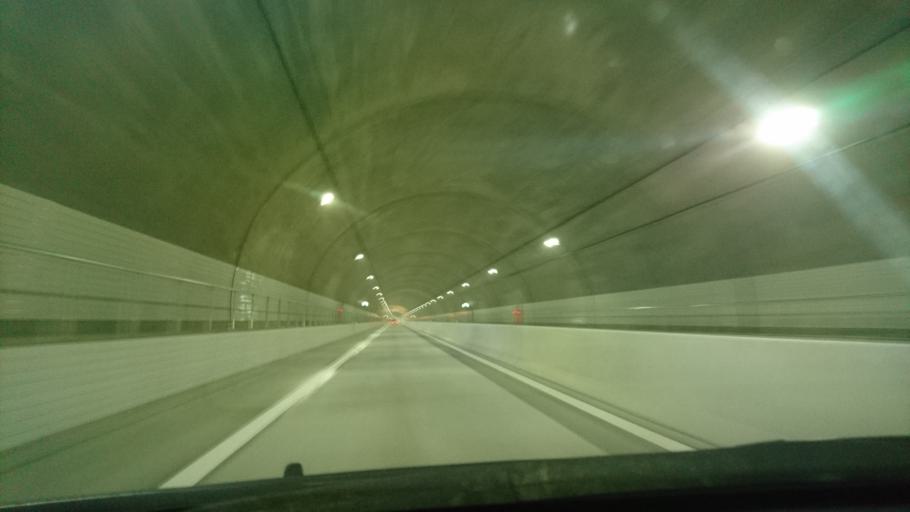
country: JP
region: Iwate
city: Kamaishi
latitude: 39.2274
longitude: 141.8609
